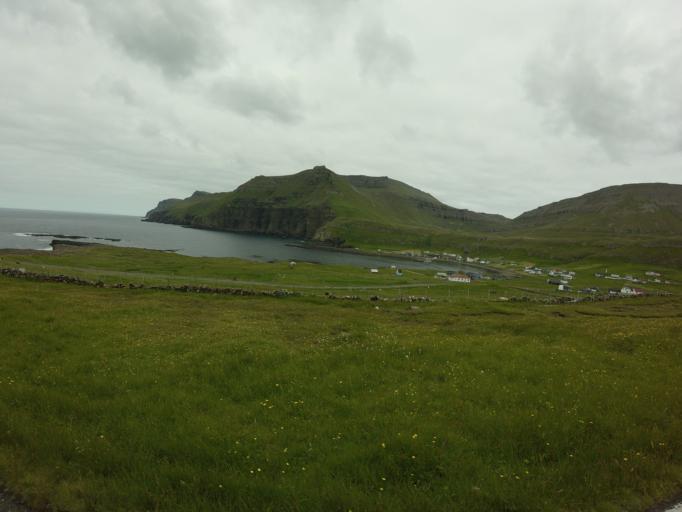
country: FO
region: Suduroy
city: Tvoroyri
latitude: 61.5191
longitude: -6.8871
